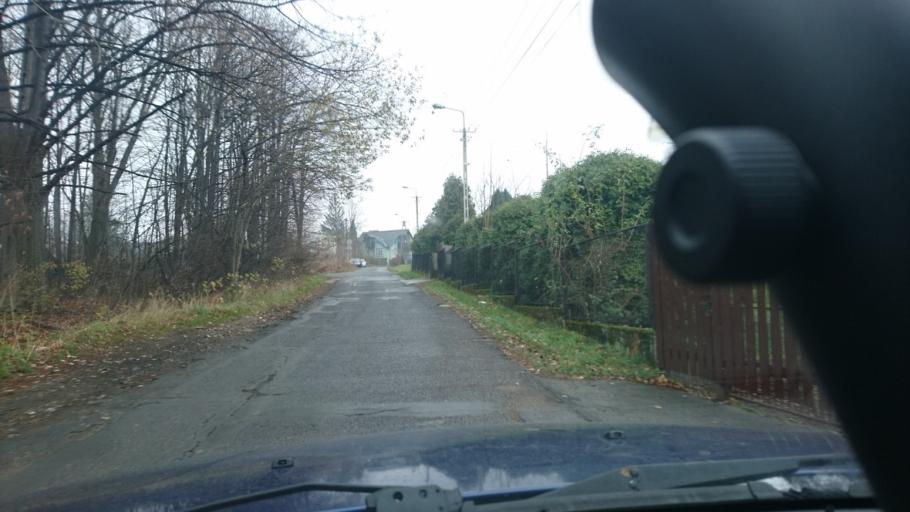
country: PL
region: Silesian Voivodeship
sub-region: Bielsko-Biala
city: Bielsko-Biala
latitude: 49.7958
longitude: 19.0681
